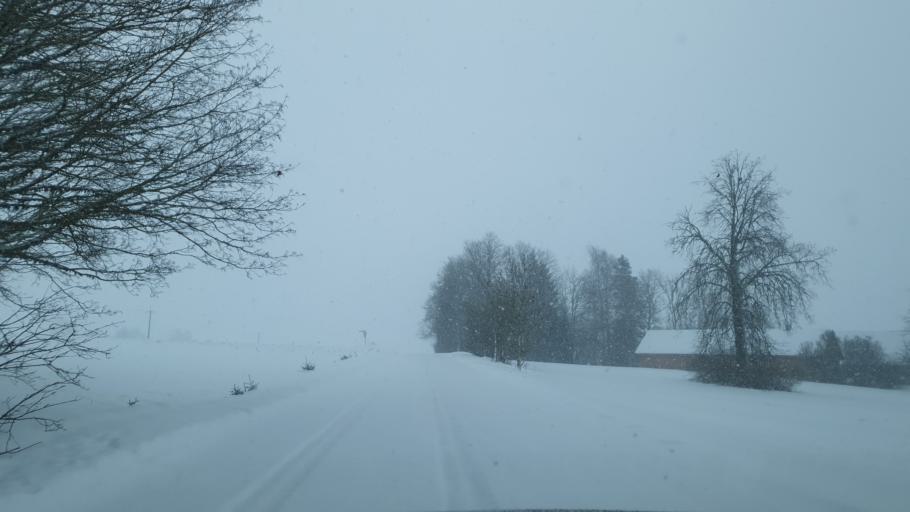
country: EE
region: Jogevamaa
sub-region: Jogeva linn
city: Jogeva
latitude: 58.7991
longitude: 26.4561
